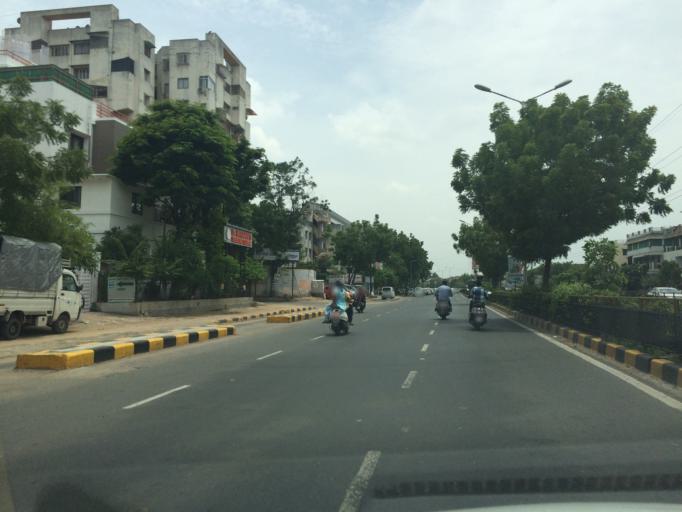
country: IN
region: Gujarat
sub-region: Ahmadabad
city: Ahmedabad
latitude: 23.0631
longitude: 72.5542
